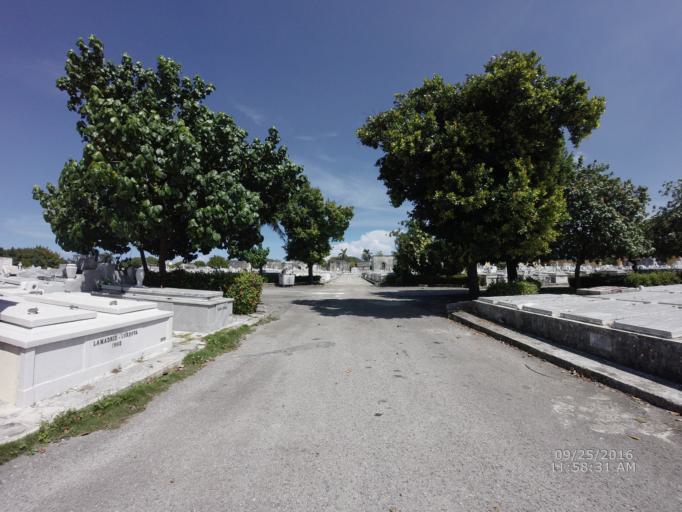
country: CU
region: La Habana
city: Havana
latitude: 23.1218
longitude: -82.3955
